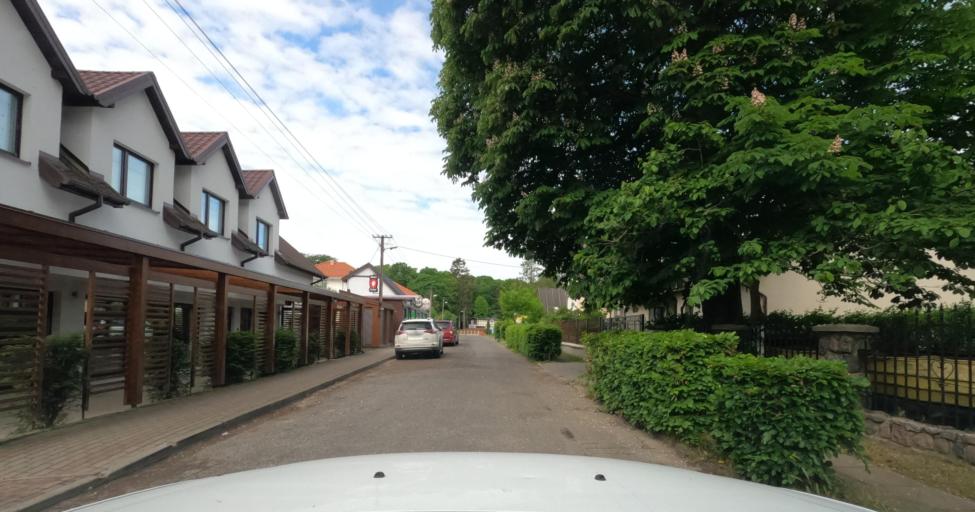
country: PL
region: West Pomeranian Voivodeship
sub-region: Powiat kamienski
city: Miedzyzdroje
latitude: 53.9669
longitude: 14.5705
